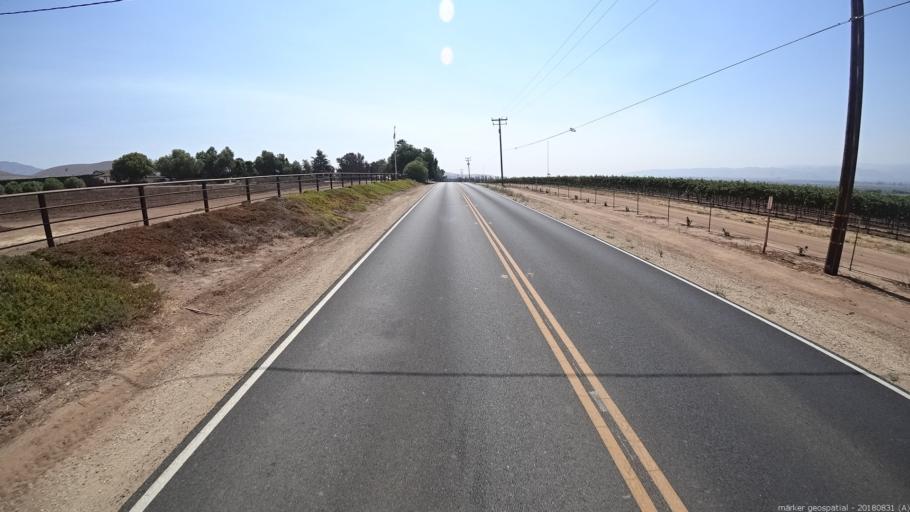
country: US
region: California
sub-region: Monterey County
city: Soledad
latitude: 36.4186
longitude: -121.2814
